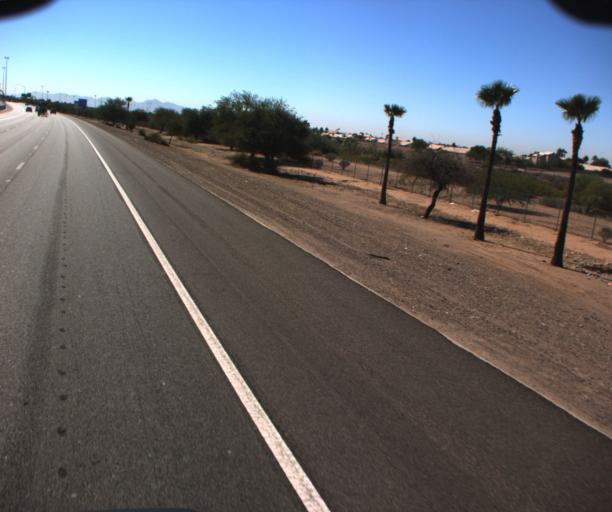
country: US
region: Arizona
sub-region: Maricopa County
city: Sun City
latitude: 33.6265
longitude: -112.2405
